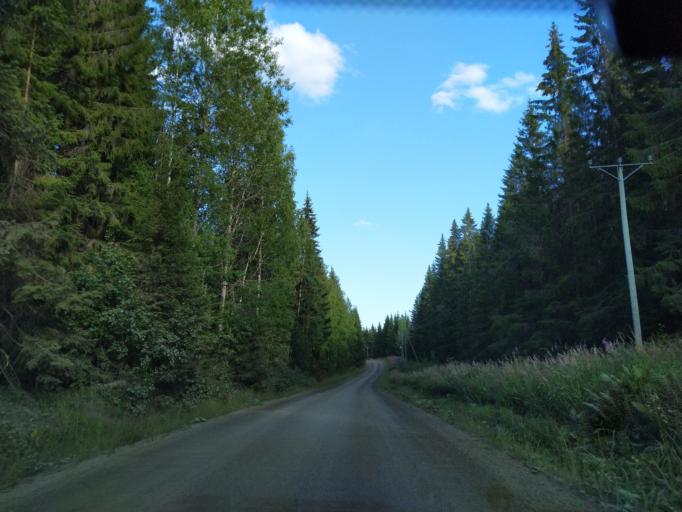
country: FI
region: Central Finland
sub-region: Jaemsae
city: Kuhmoinen
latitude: 61.6954
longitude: 24.9321
